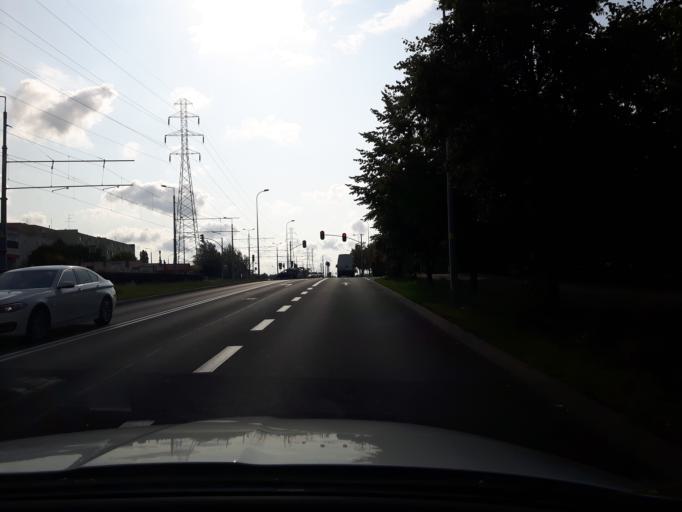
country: PL
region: Pomeranian Voivodeship
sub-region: Gdansk
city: Gdansk
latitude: 54.3383
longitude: 18.6122
